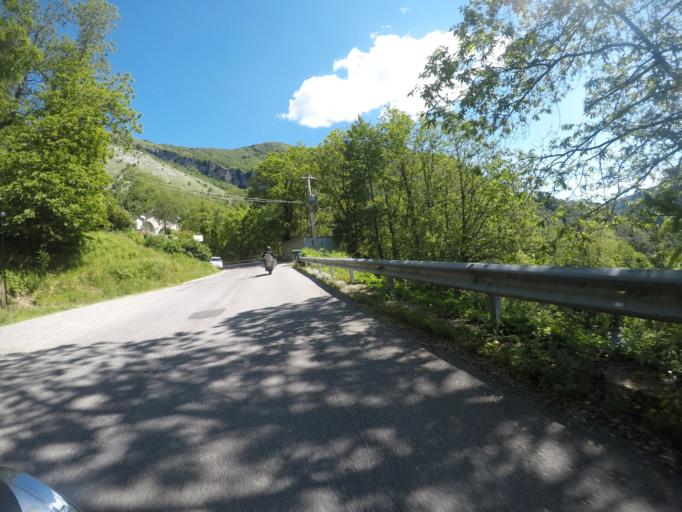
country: IT
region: Tuscany
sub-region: Provincia di Lucca
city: Fontana delle Monache
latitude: 44.0658
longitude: 10.3079
